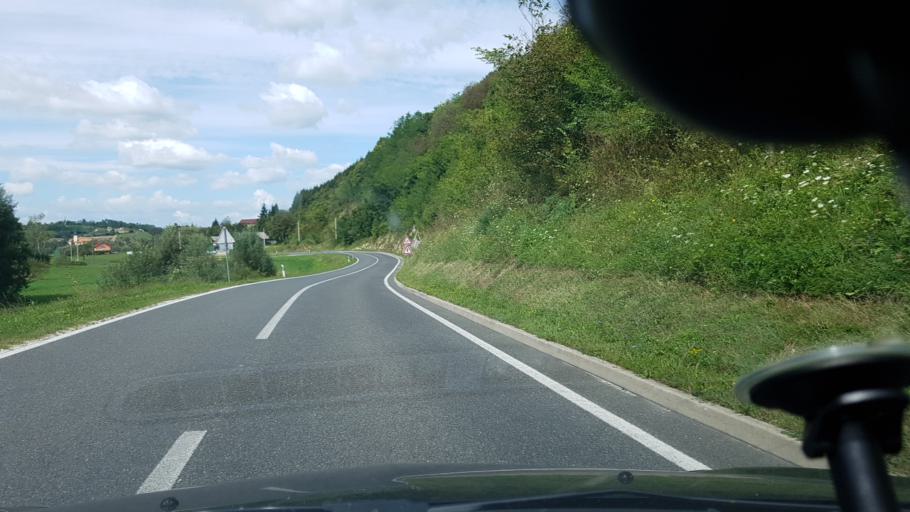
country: HR
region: Varazdinska
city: Lepoglava
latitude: 46.2188
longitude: 15.9970
